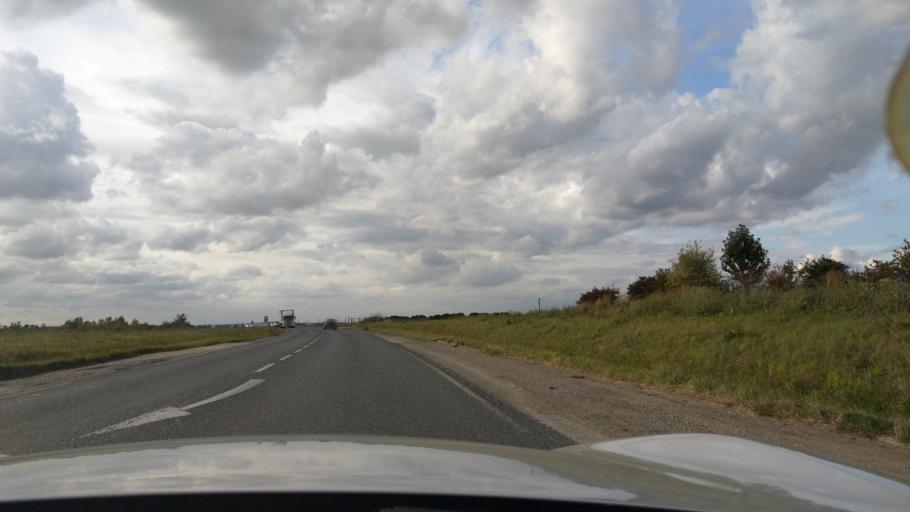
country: FR
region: Ile-de-France
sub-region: Departement du Val-d'Oise
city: Vemars
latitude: 49.0290
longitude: 2.5790
